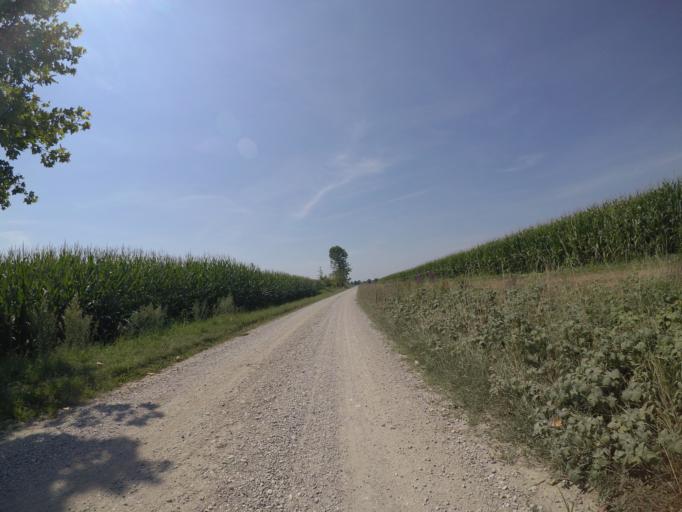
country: IT
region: Friuli Venezia Giulia
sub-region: Provincia di Udine
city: Varmo
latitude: 45.9083
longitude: 12.9884
